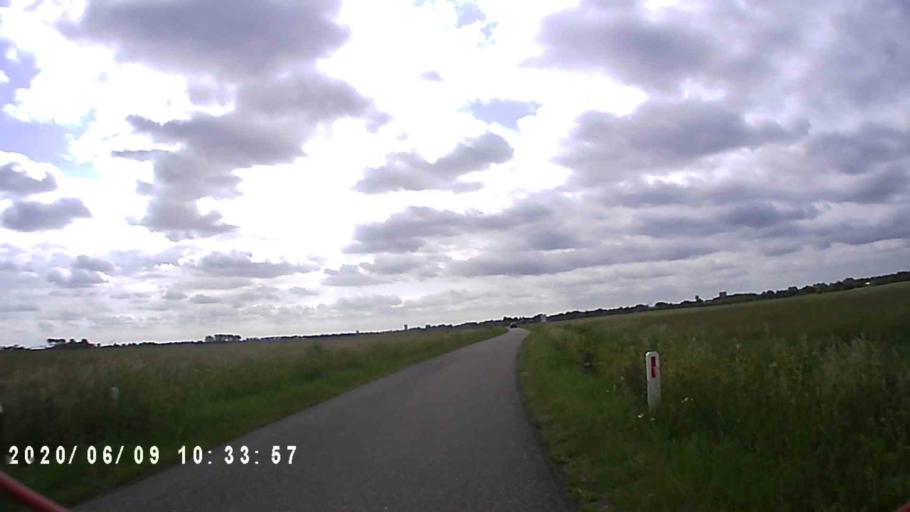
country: NL
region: Groningen
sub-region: Gemeente Zuidhorn
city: Aduard
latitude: 53.2656
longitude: 6.5156
